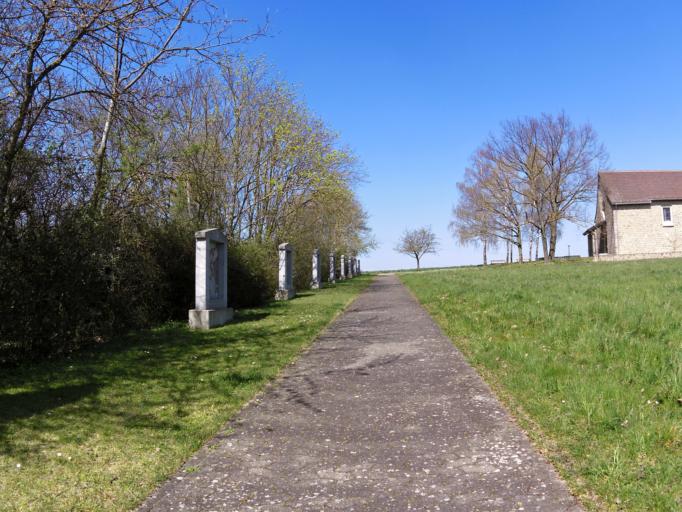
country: DE
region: Bavaria
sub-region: Regierungsbezirk Unterfranken
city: Rottendorf
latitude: 49.8132
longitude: 10.0533
